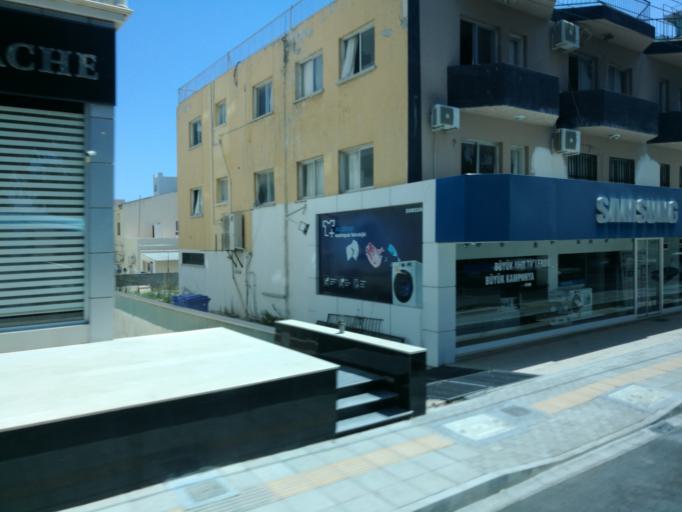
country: CY
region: Ammochostos
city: Famagusta
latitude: 35.1385
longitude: 33.9179
